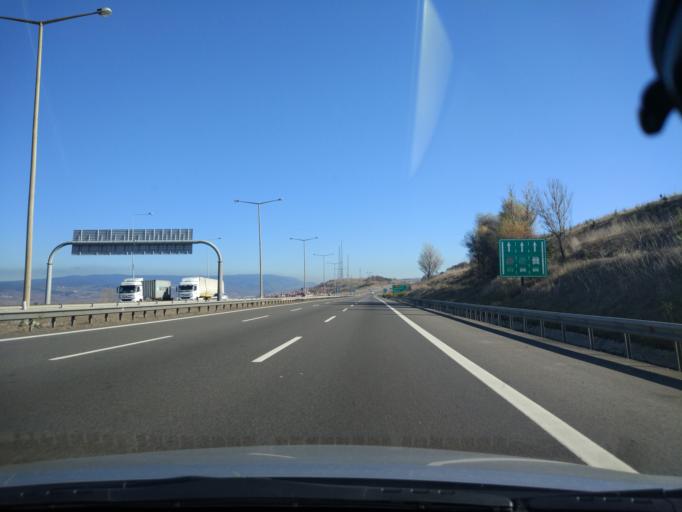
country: TR
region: Bolu
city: Yenicaga
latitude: 40.7643
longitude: 32.0155
